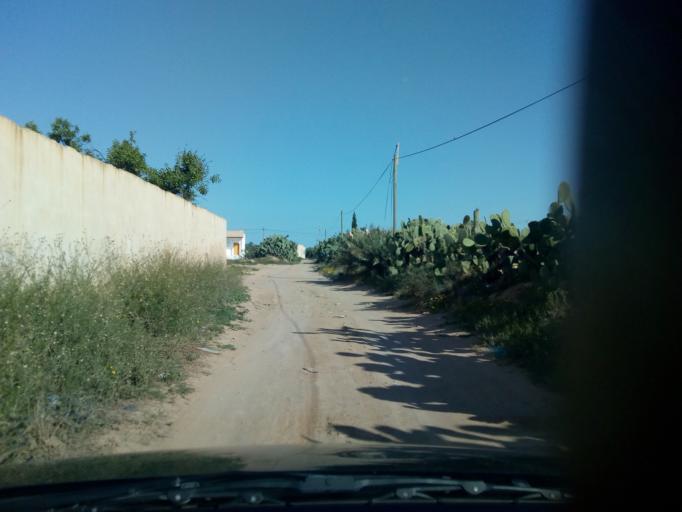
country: TN
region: Safaqis
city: Sfax
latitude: 34.7306
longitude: 10.6093
